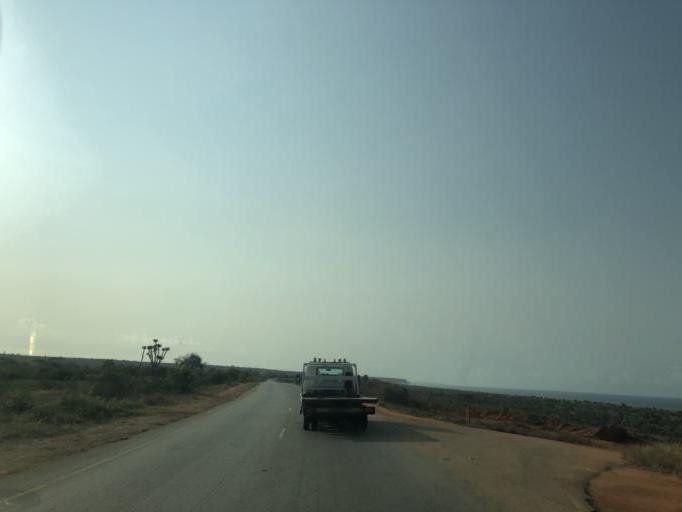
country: AO
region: Luanda
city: Luanda
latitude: -9.1641
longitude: 13.0509
